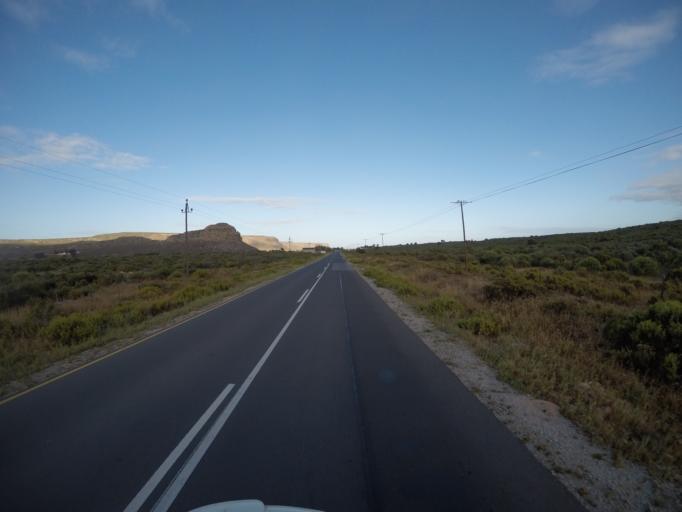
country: ZA
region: Western Cape
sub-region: West Coast District Municipality
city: Clanwilliam
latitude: -32.3127
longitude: 18.3659
